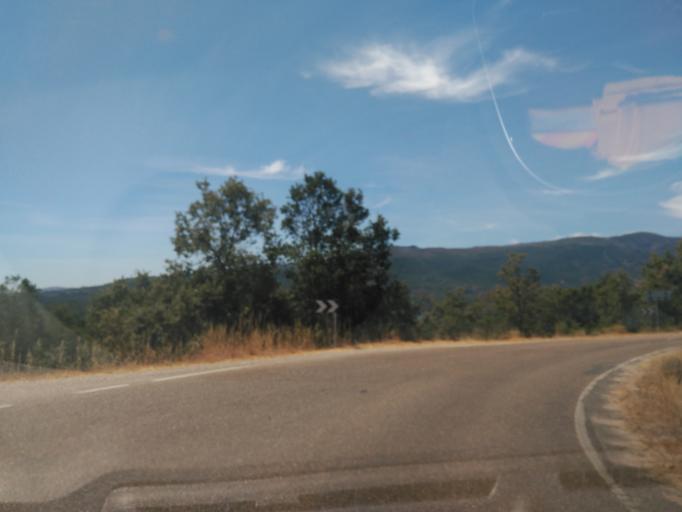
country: ES
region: Castille and Leon
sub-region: Provincia de Zamora
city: Trefacio
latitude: 42.1317
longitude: -6.6917
